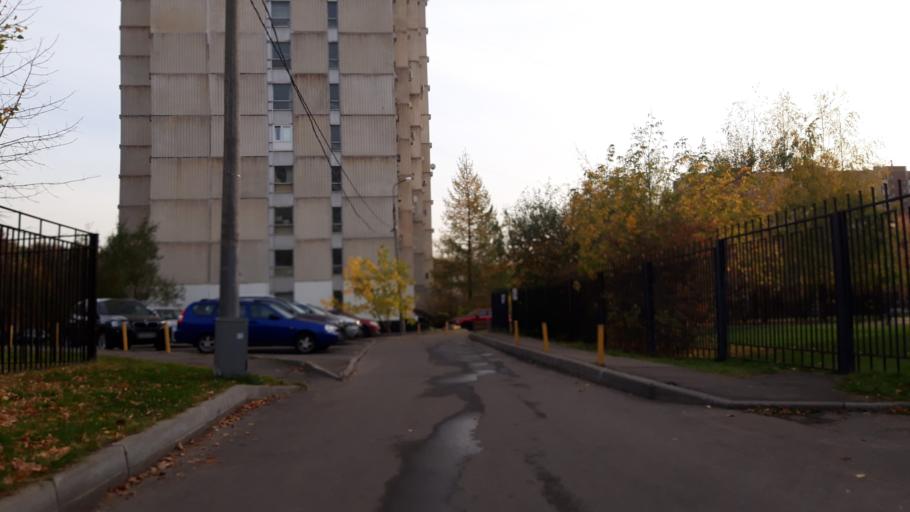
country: RU
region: Moscow
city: Zelenograd
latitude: 55.9940
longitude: 37.1725
